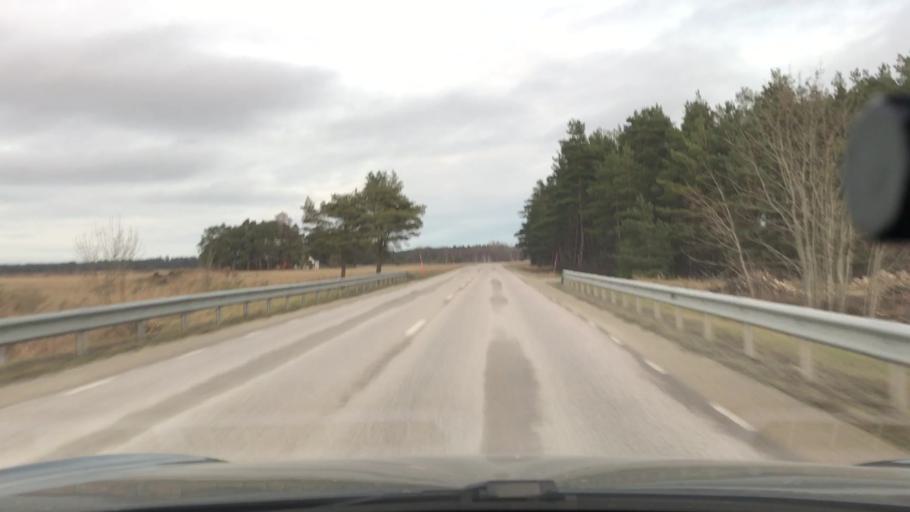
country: SE
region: Gotland
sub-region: Gotland
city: Slite
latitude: 57.7164
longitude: 18.5518
